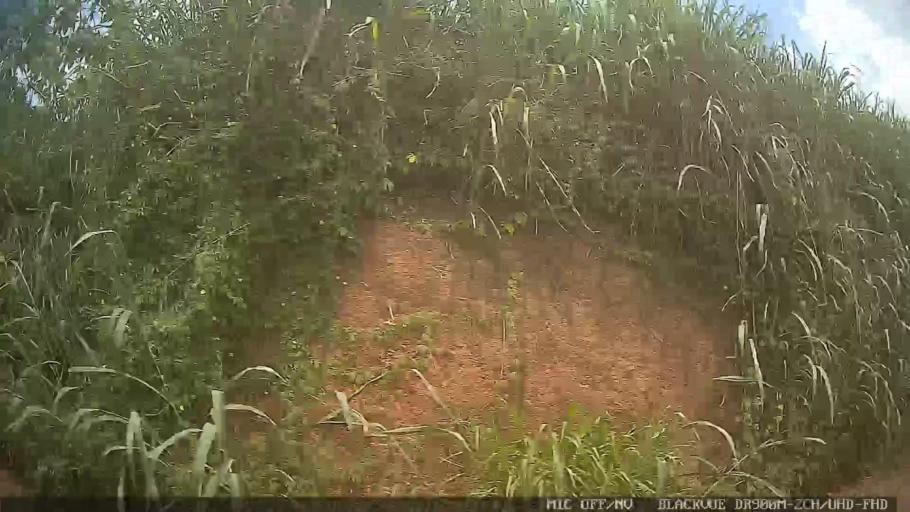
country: BR
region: Sao Paulo
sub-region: Atibaia
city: Atibaia
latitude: -23.0424
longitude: -46.5229
